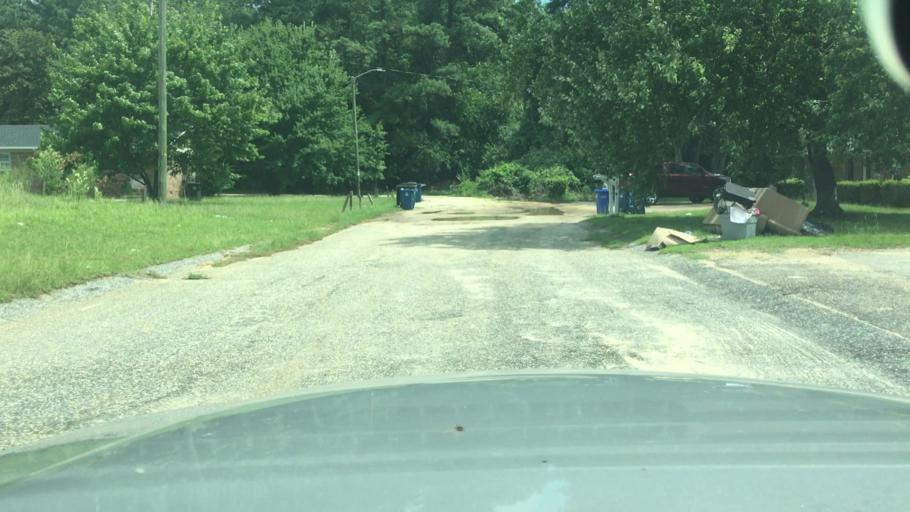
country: US
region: North Carolina
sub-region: Cumberland County
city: Hope Mills
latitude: 35.0366
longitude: -78.9938
